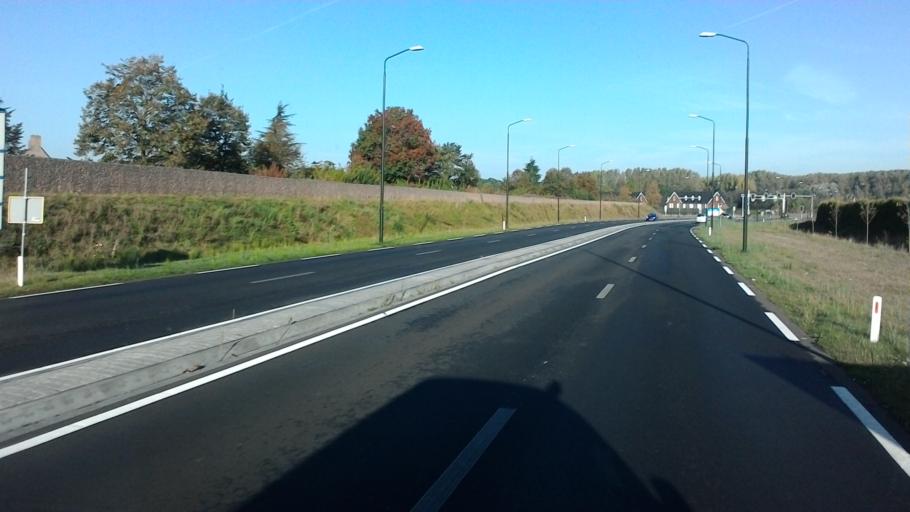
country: NL
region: North Brabant
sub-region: Gemeente Schijndel
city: Schijndel
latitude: 51.6156
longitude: 5.4567
